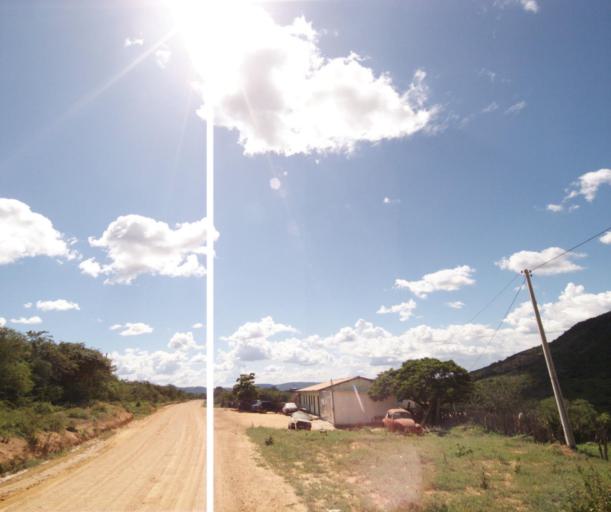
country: BR
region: Bahia
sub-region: Pocoes
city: Pocoes
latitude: -14.2516
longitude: -40.7074
